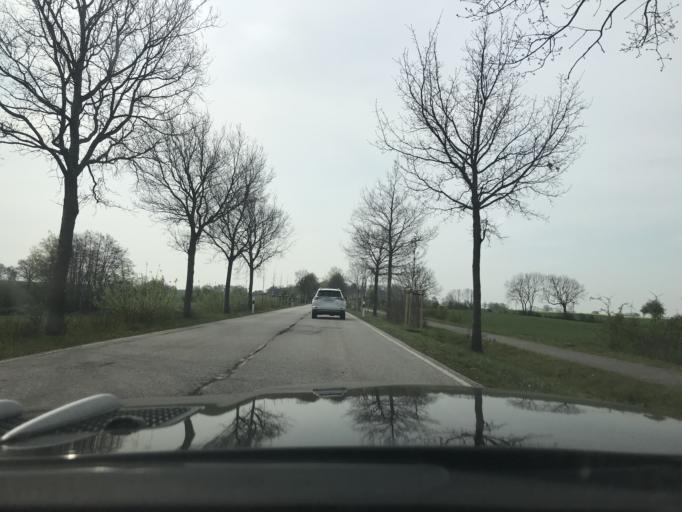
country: DE
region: Schleswig-Holstein
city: Heringsdorf
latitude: 54.2958
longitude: 11.0132
